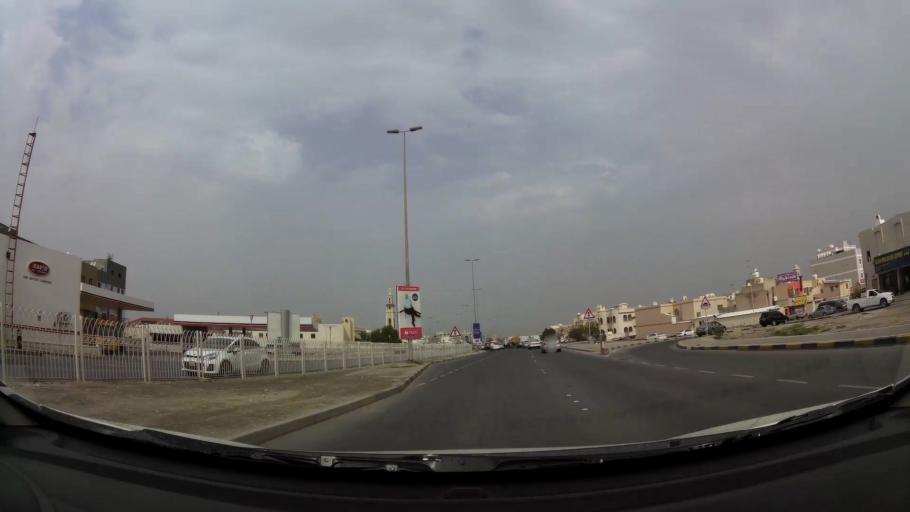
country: BH
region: Northern
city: Ar Rifa'
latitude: 26.1366
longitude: 50.5708
